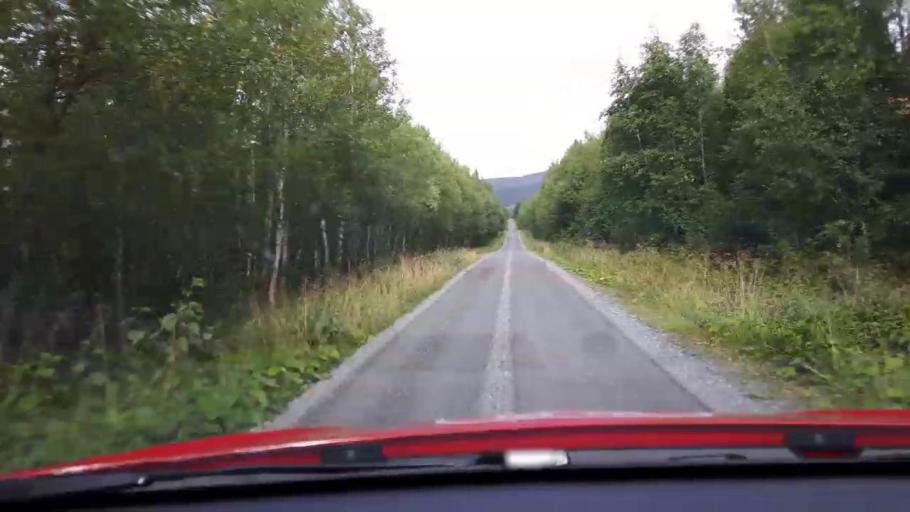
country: SE
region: Jaemtland
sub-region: Are Kommun
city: Are
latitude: 63.7921
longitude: 13.1071
